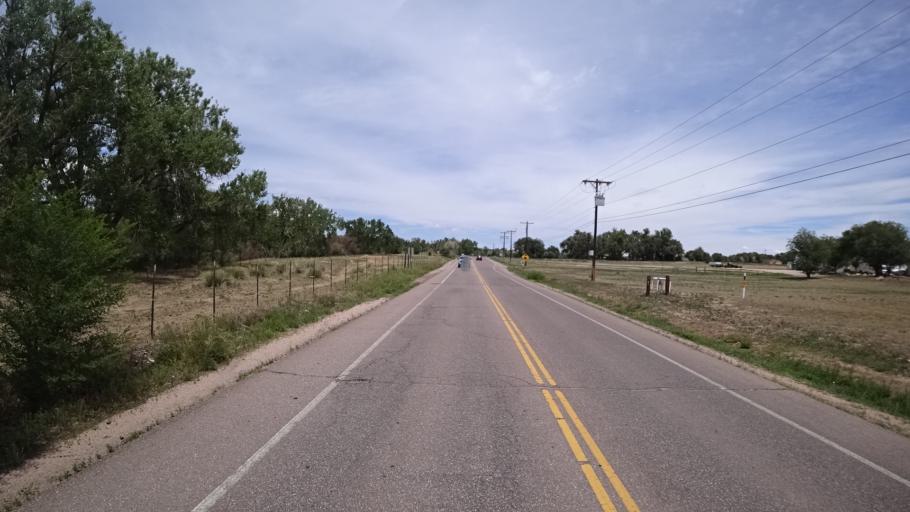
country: US
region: Colorado
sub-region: El Paso County
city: Fountain
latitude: 38.6823
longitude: -104.6876
